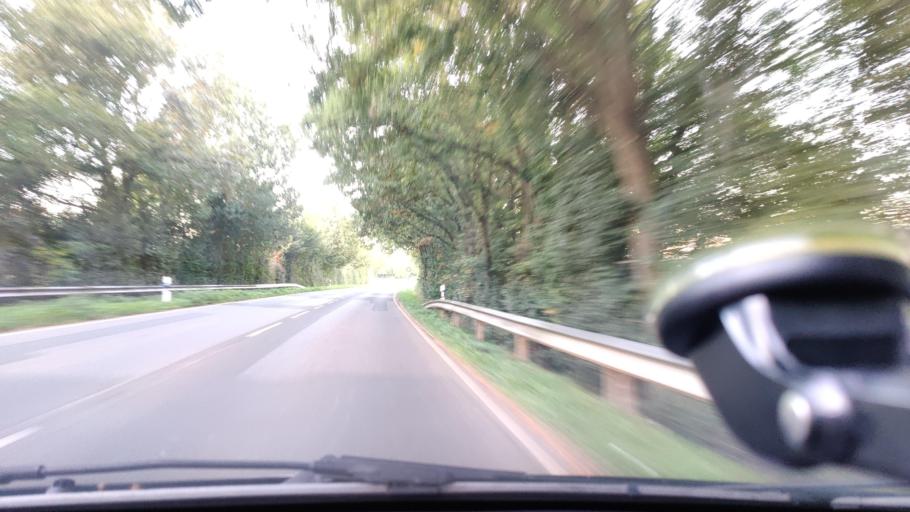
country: DE
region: North Rhine-Westphalia
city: Kalkar
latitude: 51.7366
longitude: 6.3015
